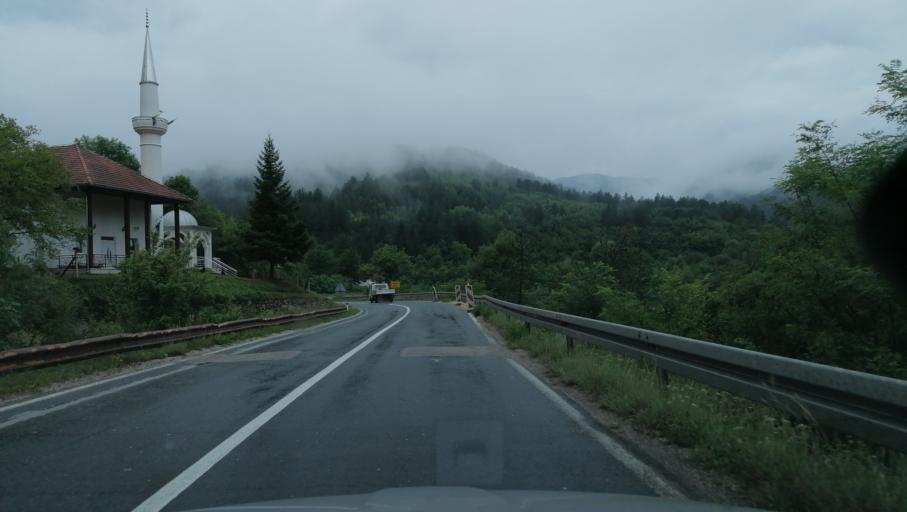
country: RS
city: Durici
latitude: 43.7496
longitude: 19.4053
